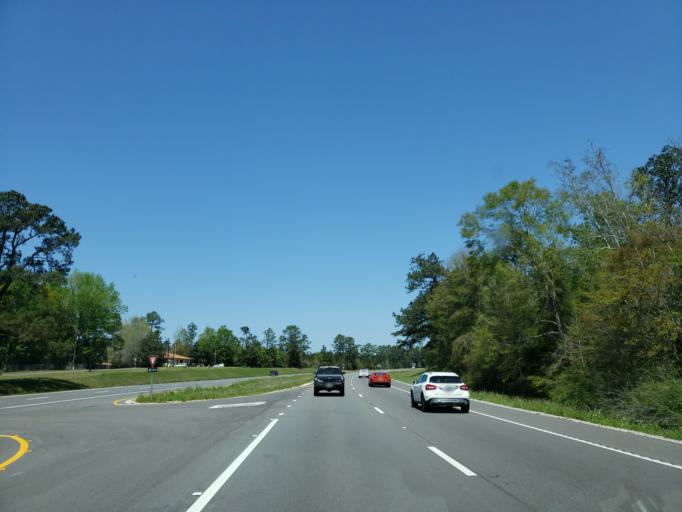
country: US
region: Mississippi
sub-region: Stone County
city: Wiggins
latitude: 30.8648
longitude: -89.1643
